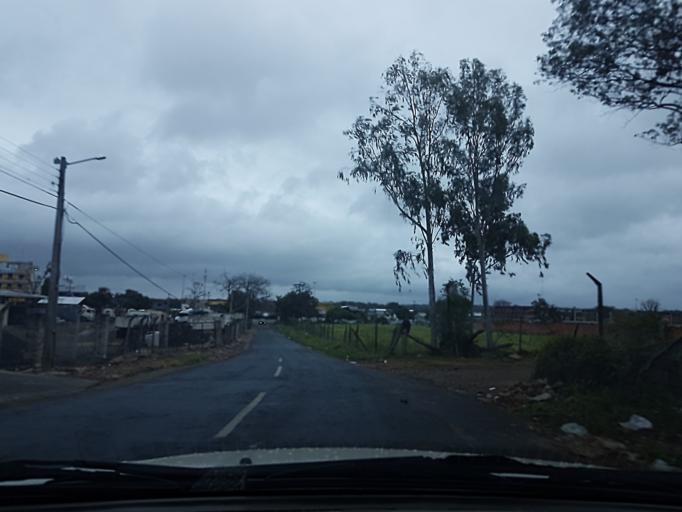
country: PY
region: Central
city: Colonia Mariano Roque Alonso
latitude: -25.2110
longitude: -57.5269
